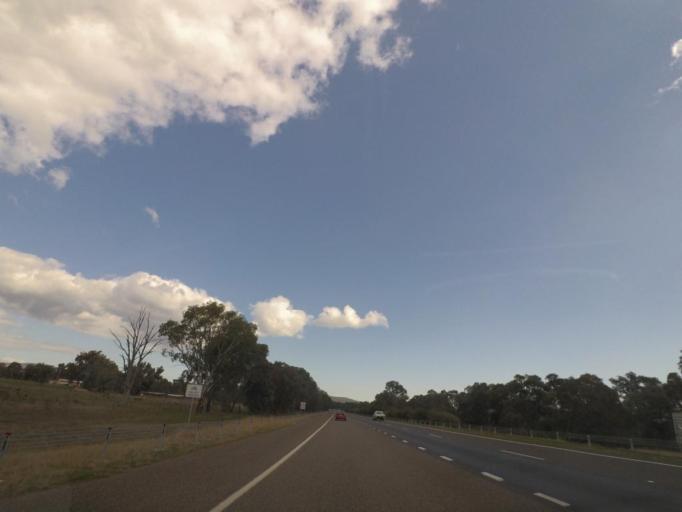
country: AU
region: New South Wales
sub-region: Corowa Shire
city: Howlong
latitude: -36.1624
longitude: 146.6020
